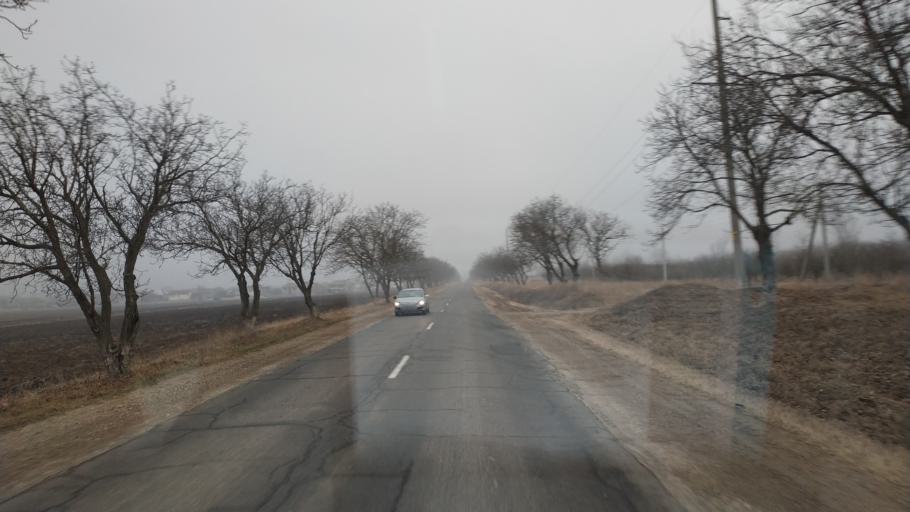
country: MD
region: Laloveni
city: Ialoveni
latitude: 46.9358
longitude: 28.8030
